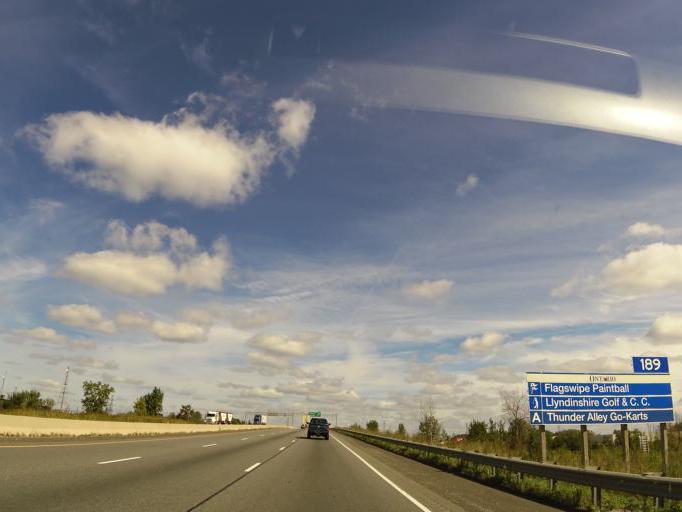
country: CA
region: Ontario
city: London
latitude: 42.9316
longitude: -81.1984
